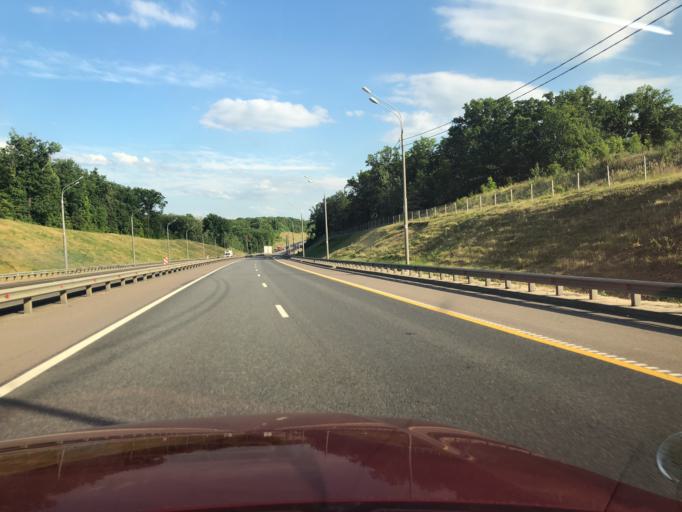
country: RU
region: Lipetsk
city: Zadonsk
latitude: 52.4085
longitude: 38.8518
